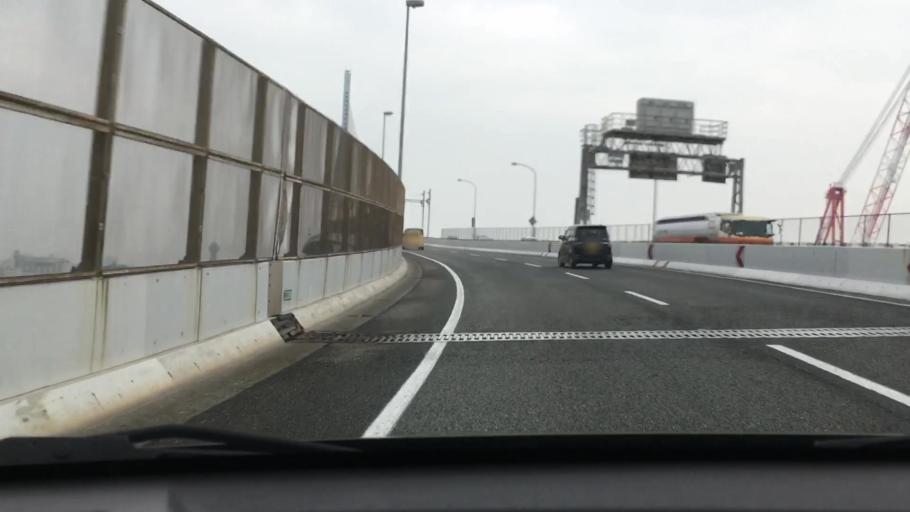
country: JP
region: Fukuoka
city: Fukuoka-shi
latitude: 33.5993
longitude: 130.3798
